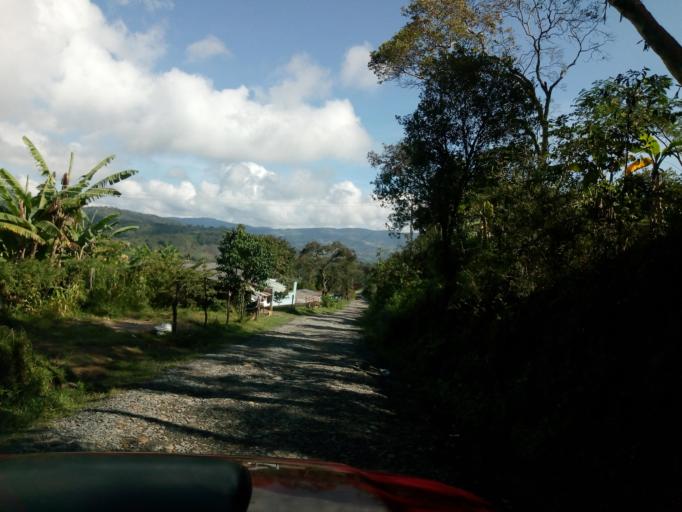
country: CO
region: Boyaca
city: Moniquira
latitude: 5.8923
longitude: -73.5357
